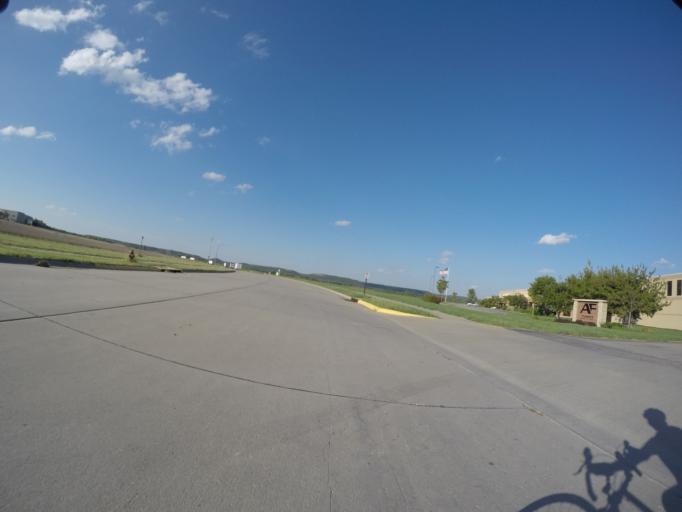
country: US
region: Kansas
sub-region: Riley County
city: Ogden
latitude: 39.1409
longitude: -96.6770
